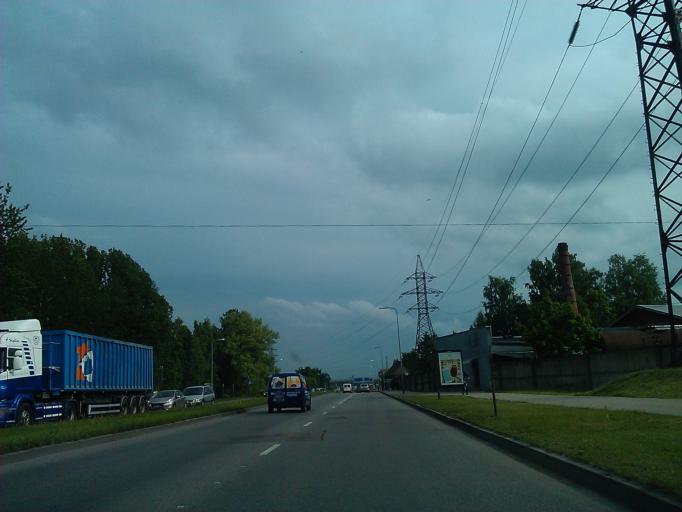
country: LV
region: Riga
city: Riga
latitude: 56.9385
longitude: 24.1730
